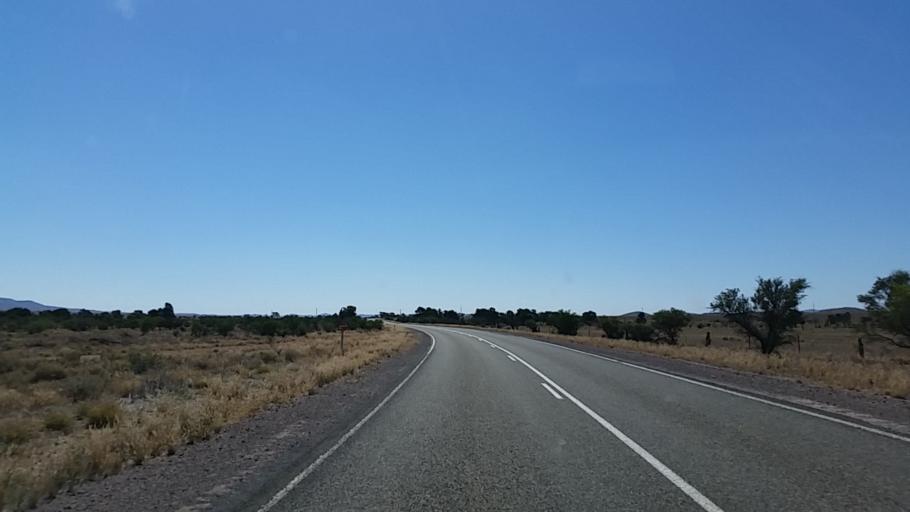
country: AU
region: South Australia
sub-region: Flinders Ranges
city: Quorn
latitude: -32.4385
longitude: 138.5354
